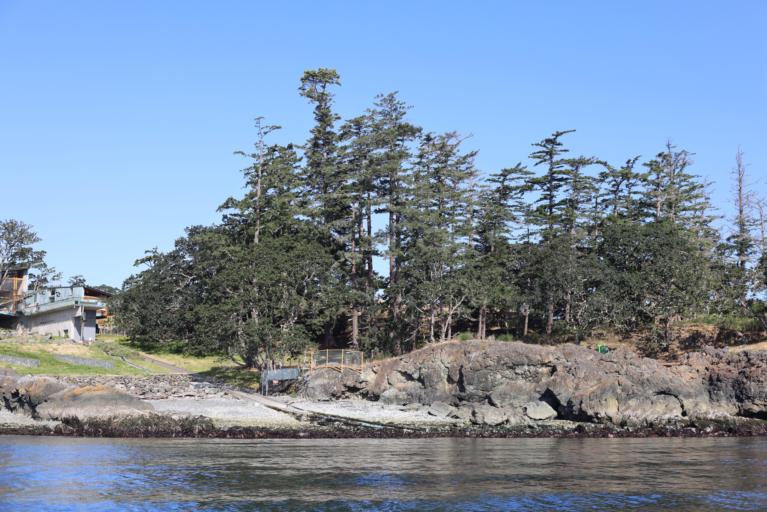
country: CA
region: British Columbia
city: Metchosin
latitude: 48.3601
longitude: -123.5343
